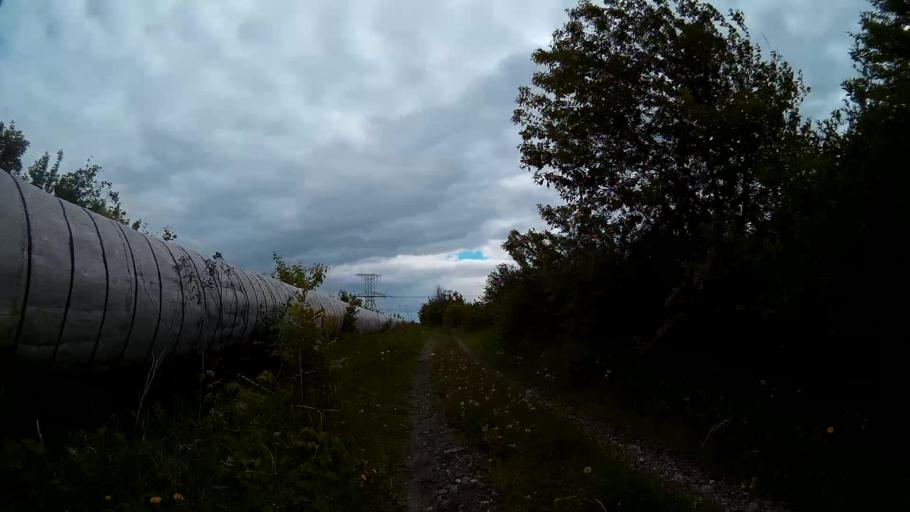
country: RU
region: Ulyanovsk
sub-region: Ulyanovskiy Rayon
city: Ulyanovsk
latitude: 54.2425
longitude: 48.2989
